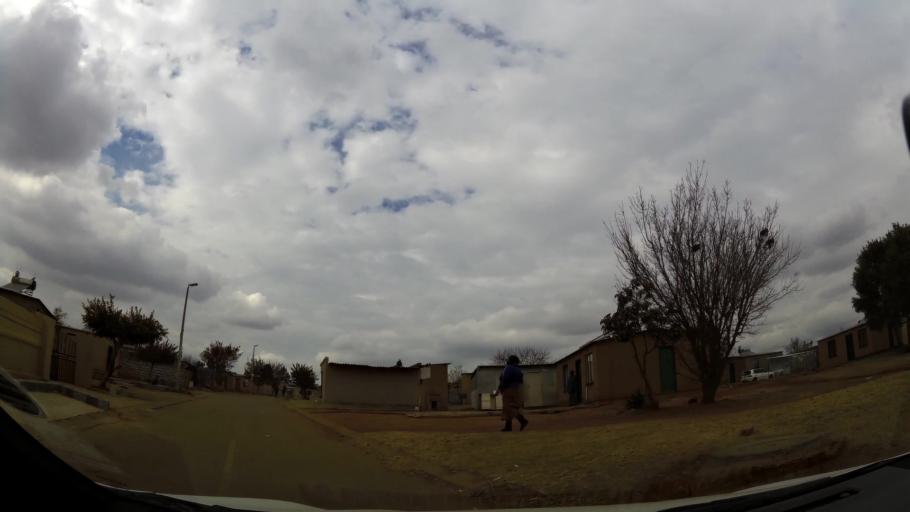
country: ZA
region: Gauteng
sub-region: Ekurhuleni Metropolitan Municipality
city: Germiston
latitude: -26.3712
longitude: 28.1197
